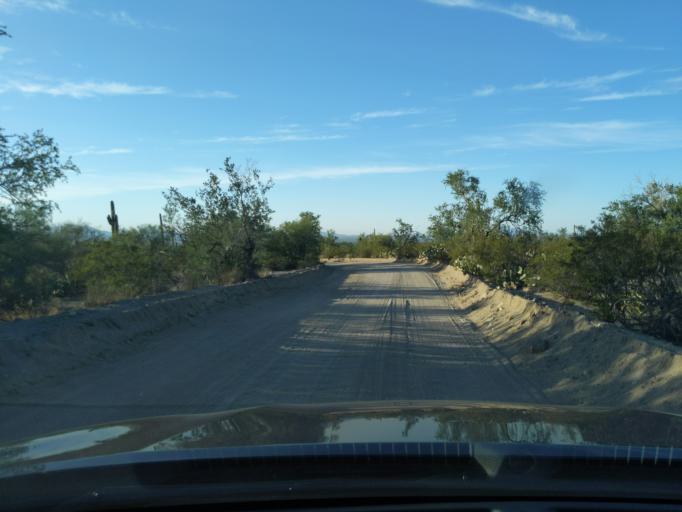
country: US
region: Arizona
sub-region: Pima County
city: Picture Rocks
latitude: 32.2875
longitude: -111.1894
